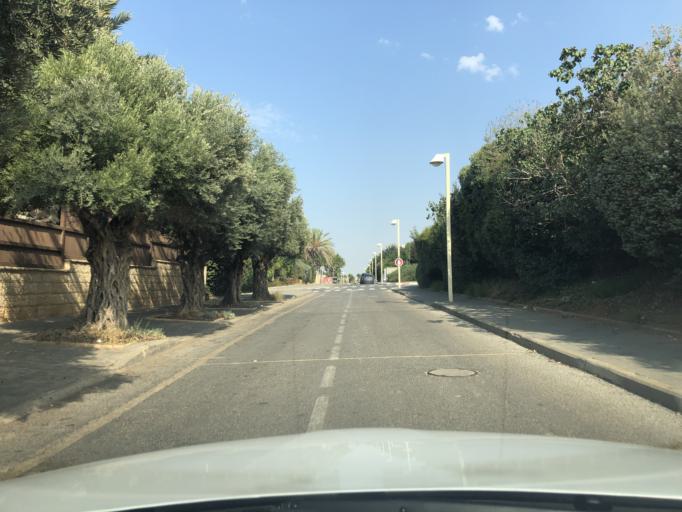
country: IL
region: Tel Aviv
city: Kefar Shemaryahu
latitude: 32.2142
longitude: 34.8174
